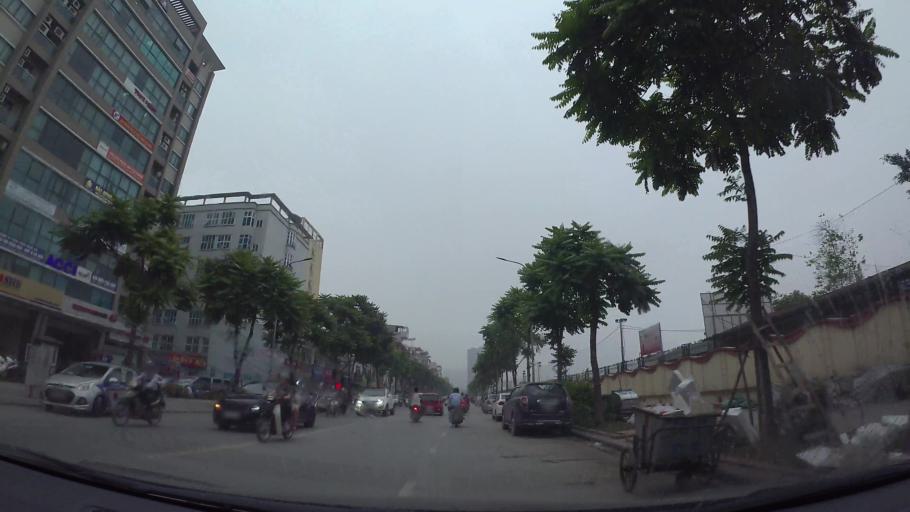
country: VN
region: Ha Noi
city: Hai BaTrung
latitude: 20.9925
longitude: 105.8324
